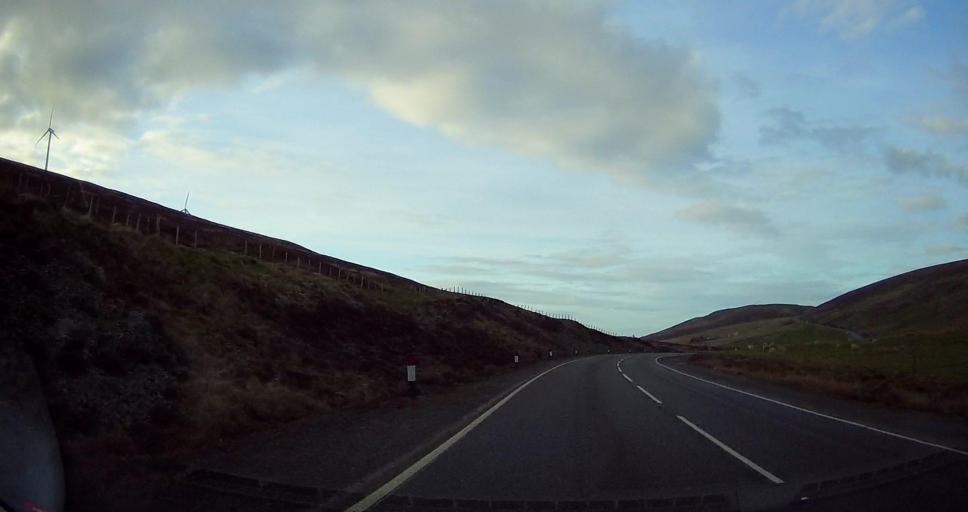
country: GB
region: Scotland
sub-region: Shetland Islands
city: Lerwick
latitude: 60.1576
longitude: -1.2329
